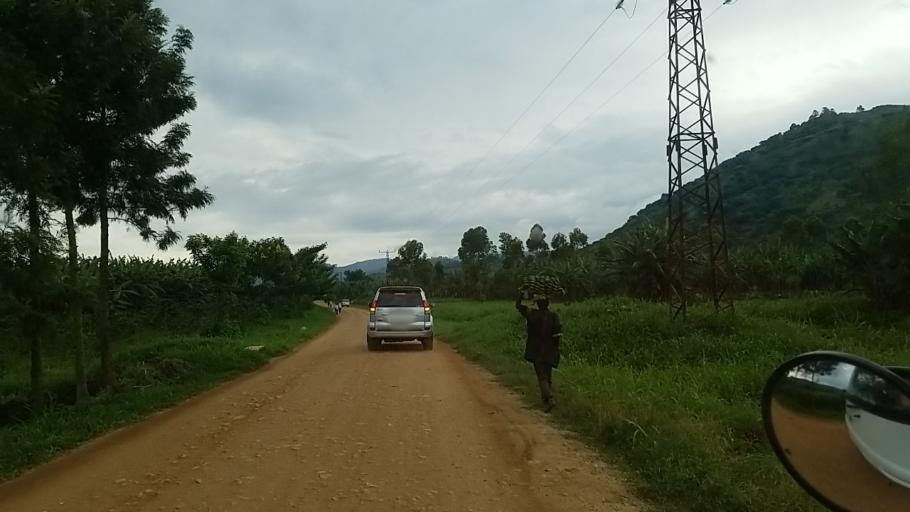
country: CD
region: Nord Kivu
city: Sake
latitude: -1.6790
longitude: 29.0165
